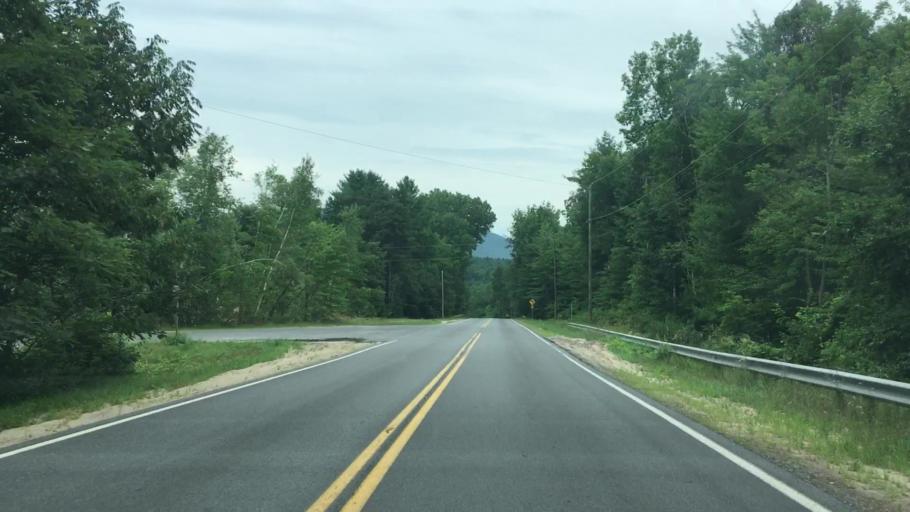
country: US
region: New York
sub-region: Essex County
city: Keeseville
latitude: 44.4687
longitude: -73.5915
